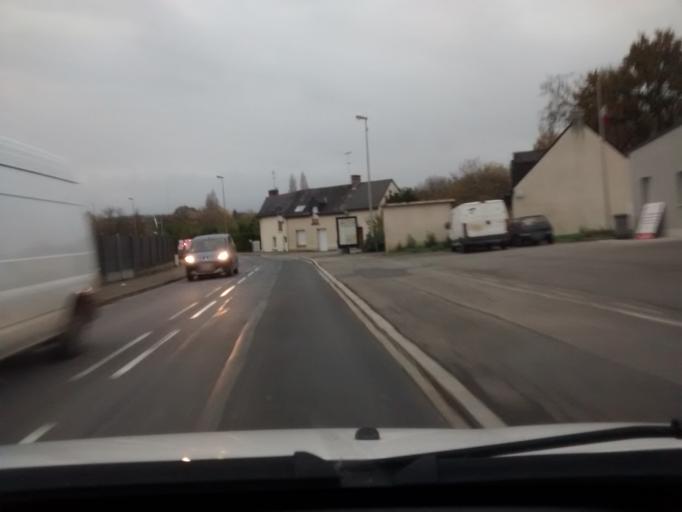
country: FR
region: Brittany
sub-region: Departement d'Ille-et-Vilaine
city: Acigne
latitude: 48.1352
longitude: -1.5428
